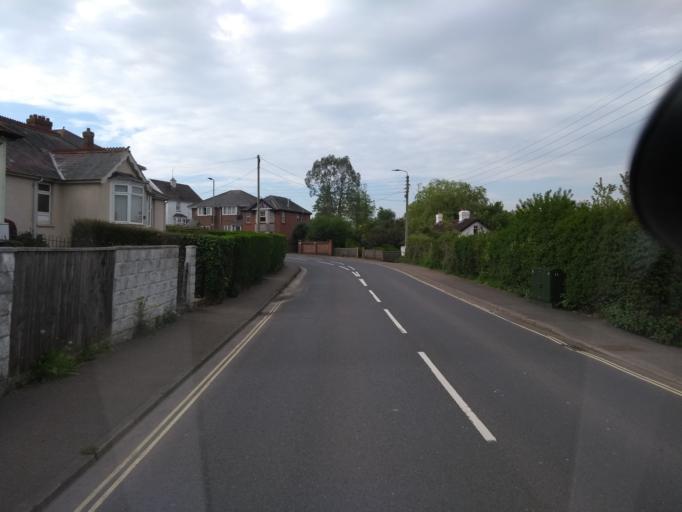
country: GB
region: England
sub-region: Devon
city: Axminster
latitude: 50.7788
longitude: -3.0030
